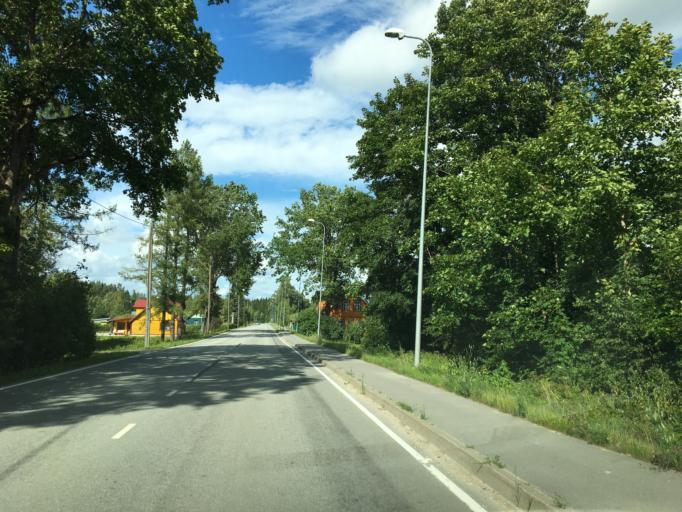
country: EE
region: Paernumaa
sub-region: Vaendra vald (alev)
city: Vandra
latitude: 58.6195
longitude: 25.1036
